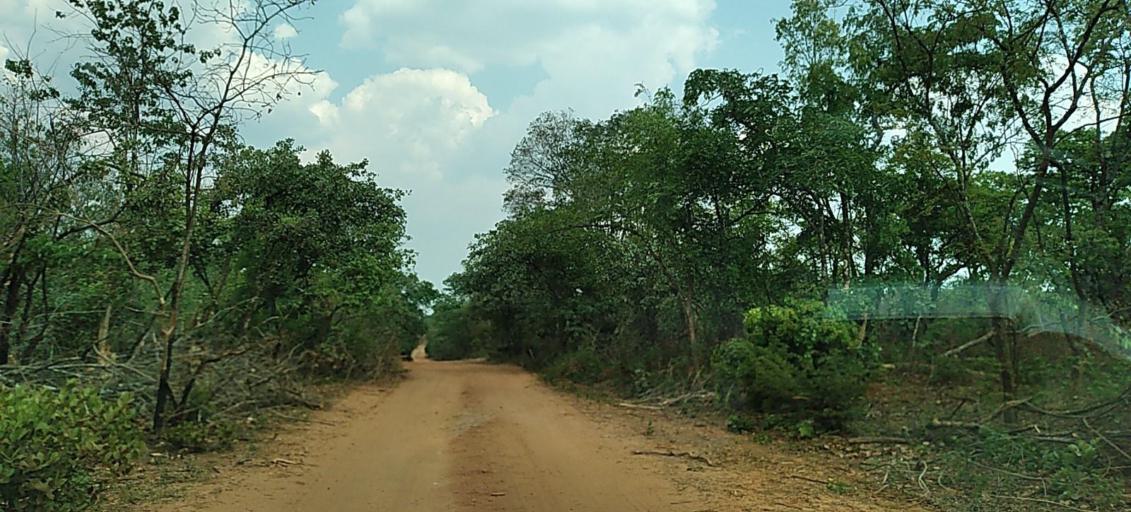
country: ZM
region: Copperbelt
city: Chingola
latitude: -12.7393
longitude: 27.7710
